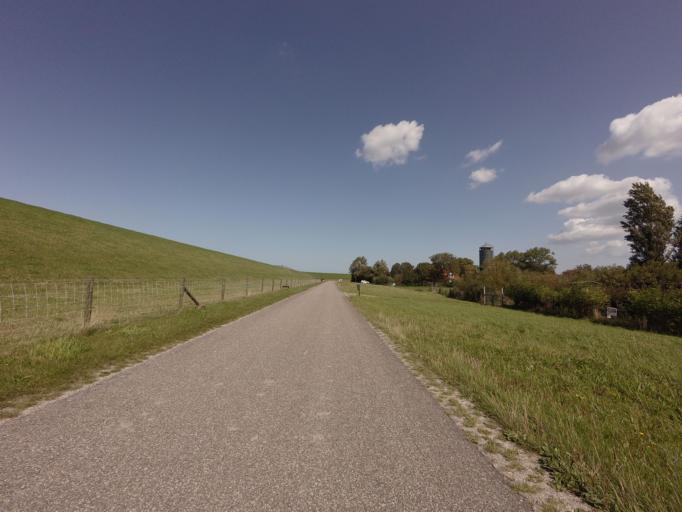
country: NL
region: Friesland
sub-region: Gemeente Ferwerderadiel
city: Hallum
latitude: 53.3274
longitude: 5.7706
